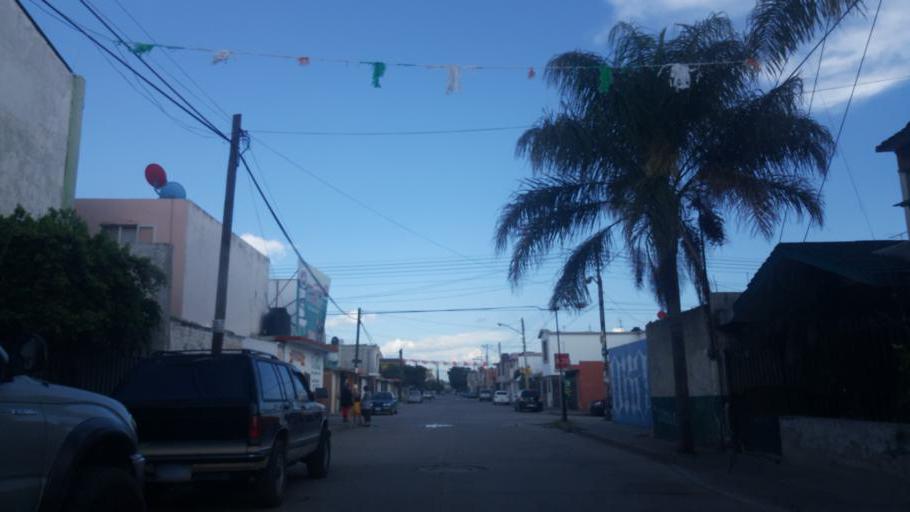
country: MX
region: Guanajuato
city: Leon
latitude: 21.1011
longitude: -101.7023
